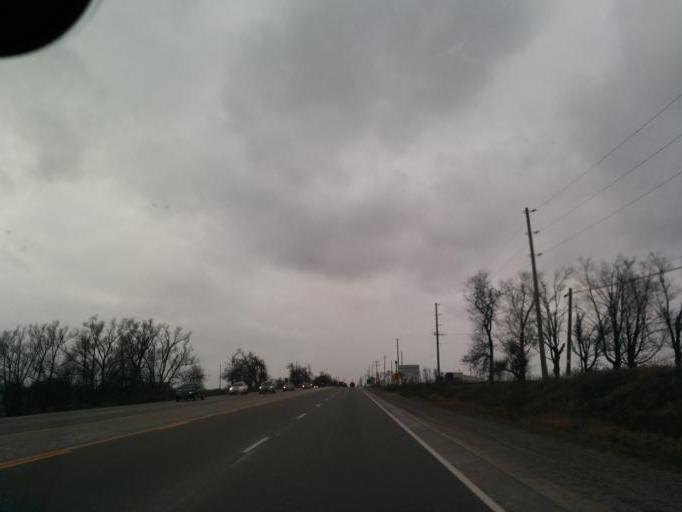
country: CA
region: Ontario
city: Brampton
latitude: 43.7510
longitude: -79.8479
